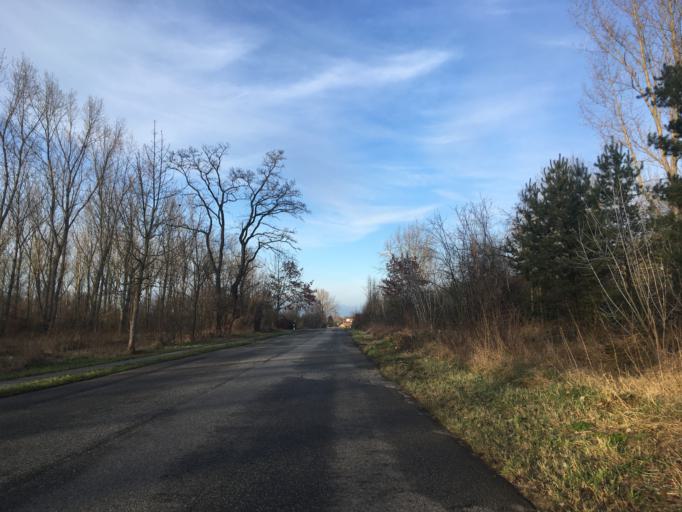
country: DE
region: Berlin
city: Blankenfelde
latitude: 52.6349
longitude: 13.4010
